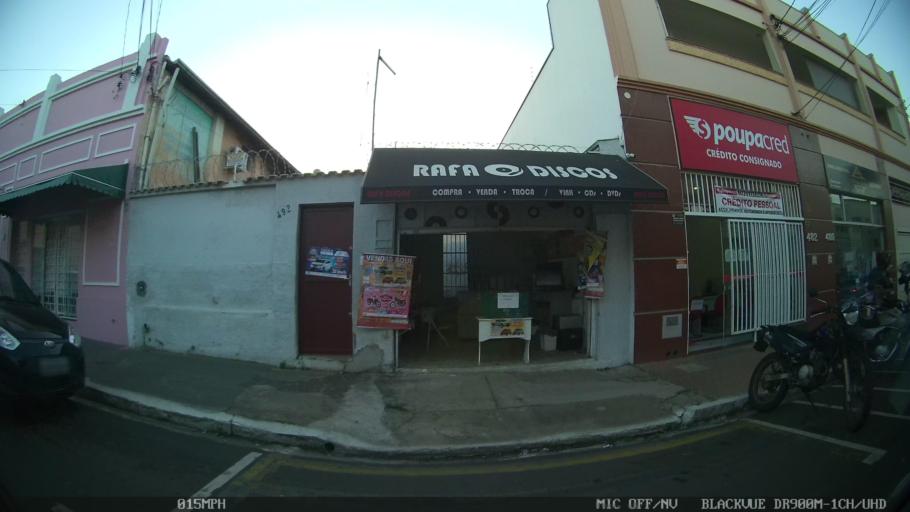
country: BR
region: Sao Paulo
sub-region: Santa Barbara D'Oeste
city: Santa Barbara d'Oeste
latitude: -22.7544
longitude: -47.4125
